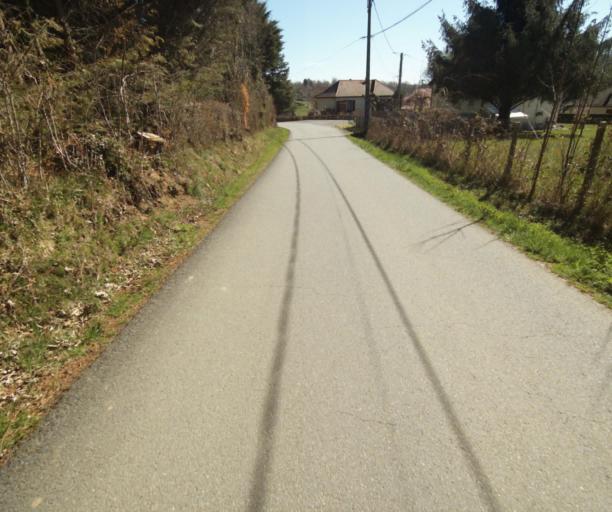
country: FR
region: Limousin
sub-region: Departement de la Correze
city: Chamboulive
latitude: 45.4296
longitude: 1.7112
